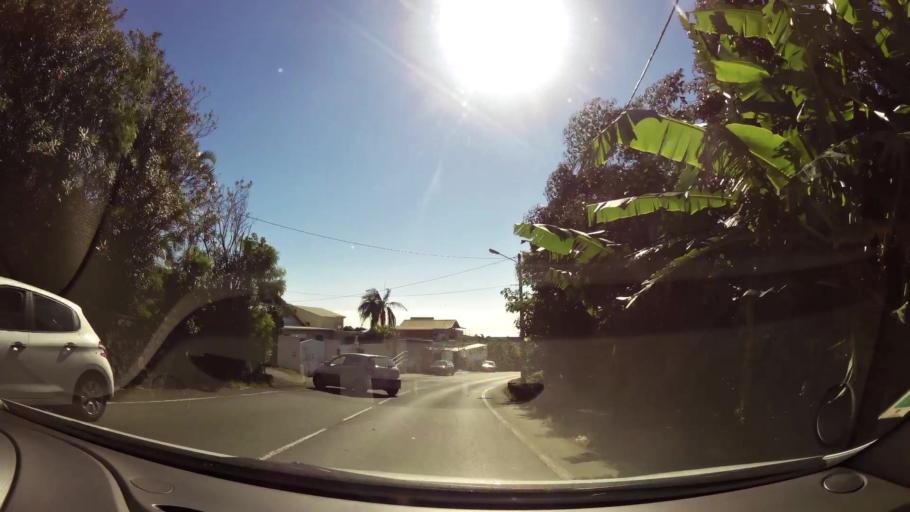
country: RE
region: Reunion
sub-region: Reunion
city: Saint-Denis
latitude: -20.9131
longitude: 55.4837
